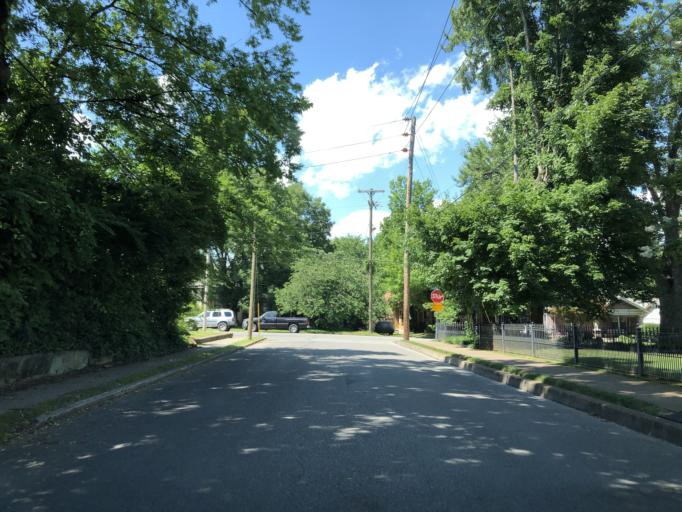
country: US
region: Tennessee
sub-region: Davidson County
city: Nashville
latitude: 36.1748
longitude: -86.7396
